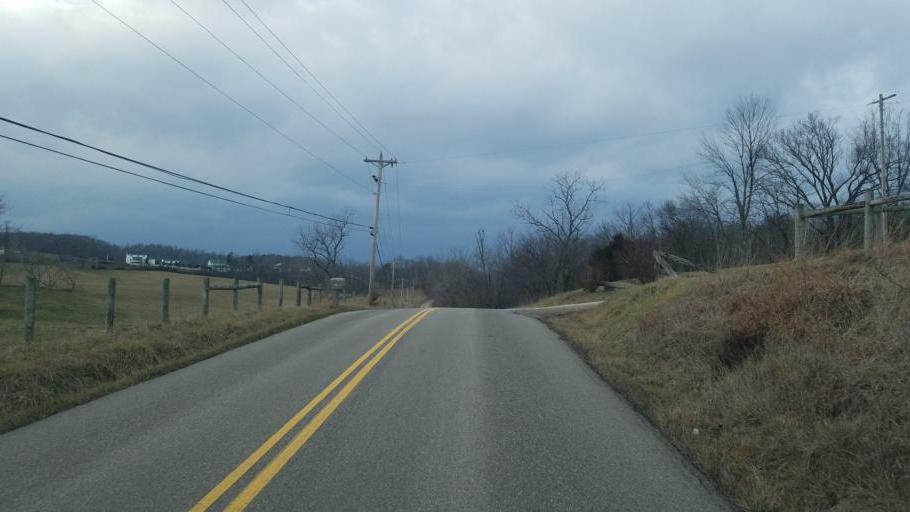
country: US
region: Ohio
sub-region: Gallia County
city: Gallipolis
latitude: 38.7650
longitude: -82.3736
